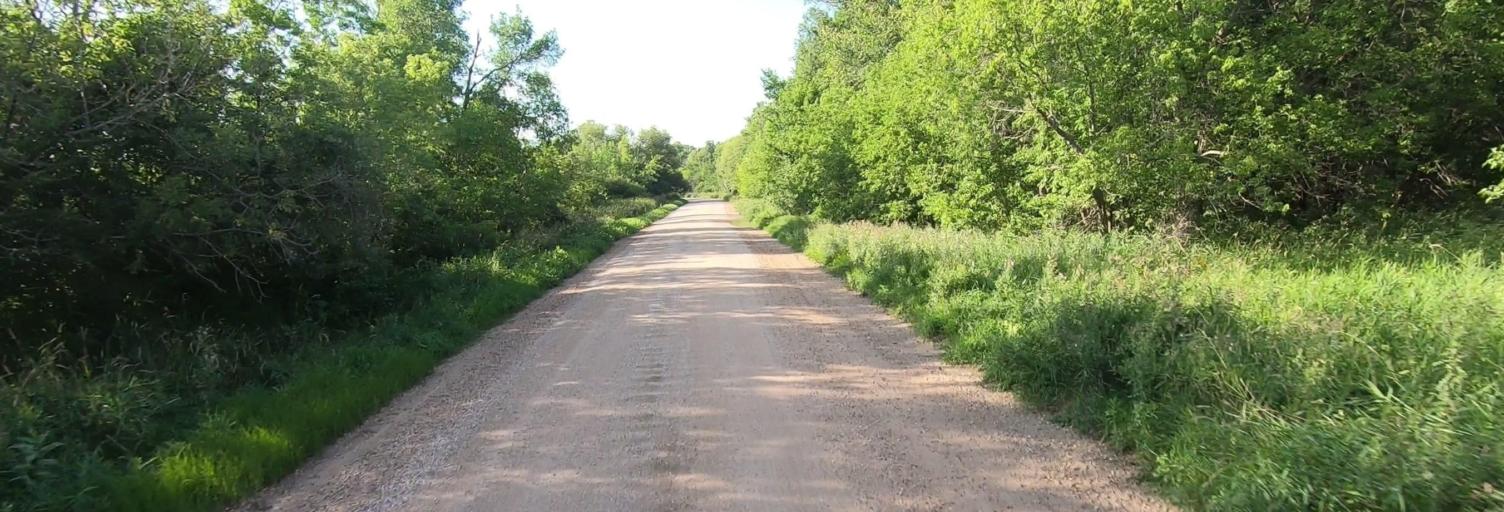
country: CA
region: Manitoba
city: Selkirk
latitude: 50.2776
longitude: -96.8522
